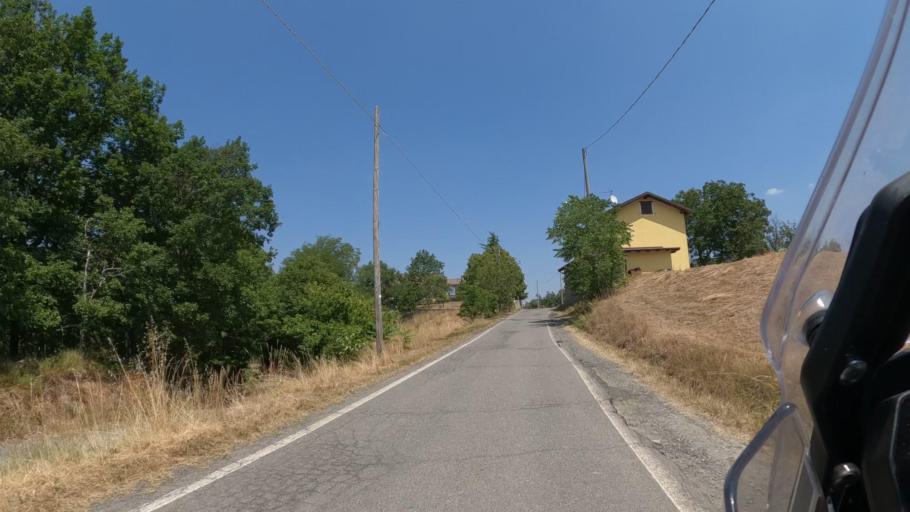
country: IT
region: Piedmont
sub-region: Provincia di Alessandria
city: Morbello
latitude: 44.5721
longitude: 8.5193
